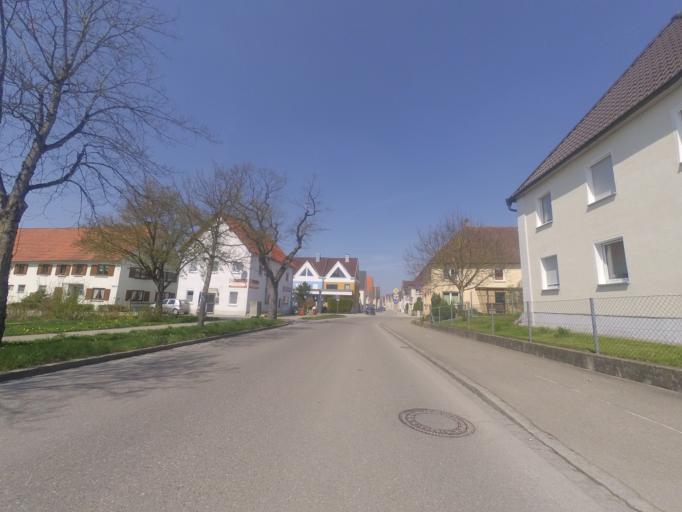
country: DE
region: Bavaria
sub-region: Swabia
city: Weissenhorn
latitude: 48.2998
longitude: 10.1605
